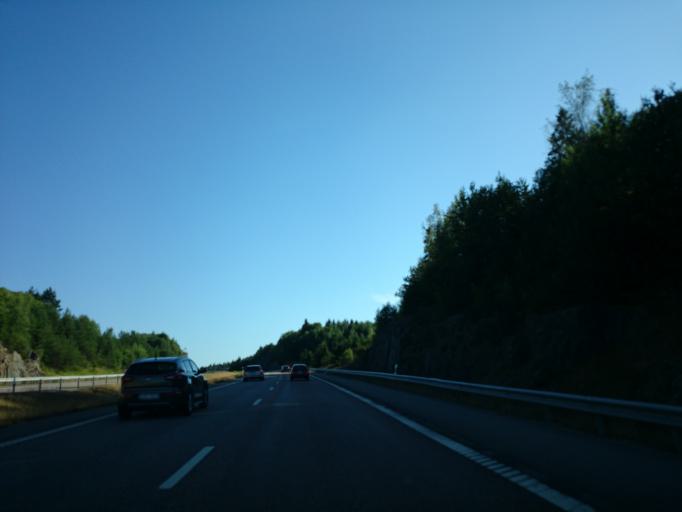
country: SE
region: Soedermanland
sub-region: Trosa Kommun
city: Vagnharad
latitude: 59.0012
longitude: 17.5382
